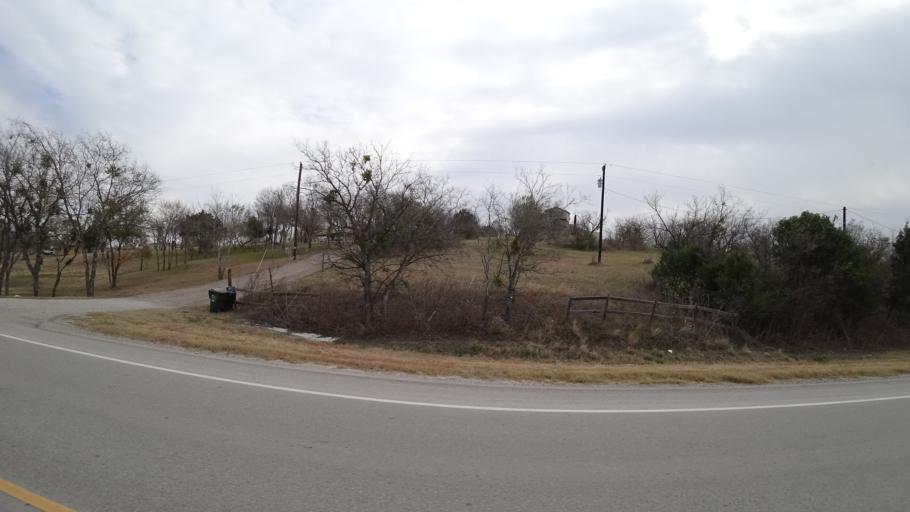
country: US
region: Texas
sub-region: Travis County
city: Onion Creek
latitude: 30.1319
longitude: -97.6828
